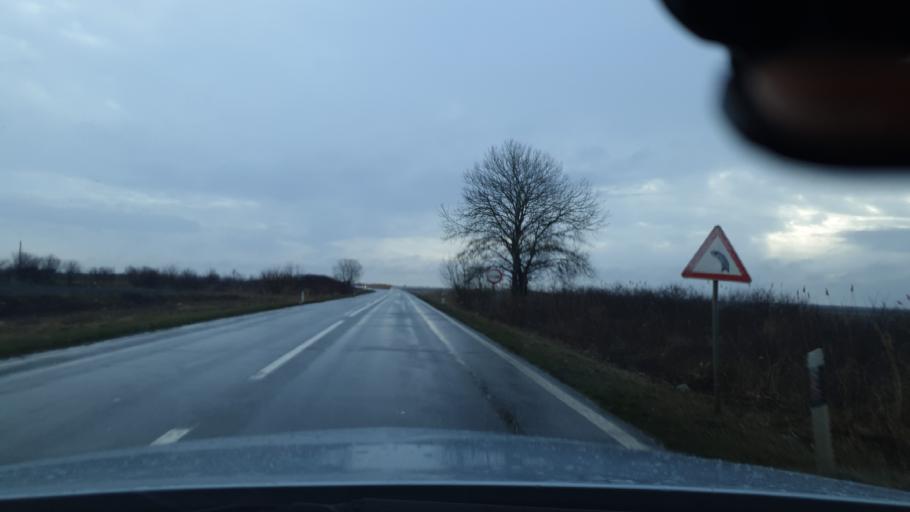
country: RS
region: Autonomna Pokrajina Vojvodina
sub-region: Juznobanatski Okrug
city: Pancevo
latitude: 44.8391
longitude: 20.8038
